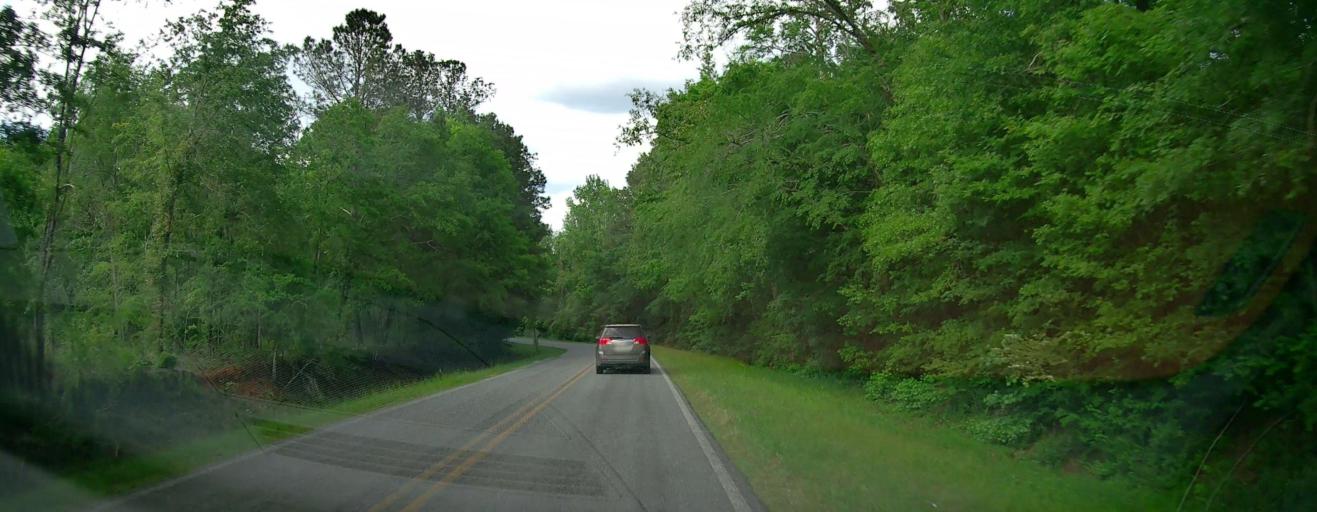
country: US
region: Georgia
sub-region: Laurens County
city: East Dublin
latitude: 32.6648
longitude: -82.8952
